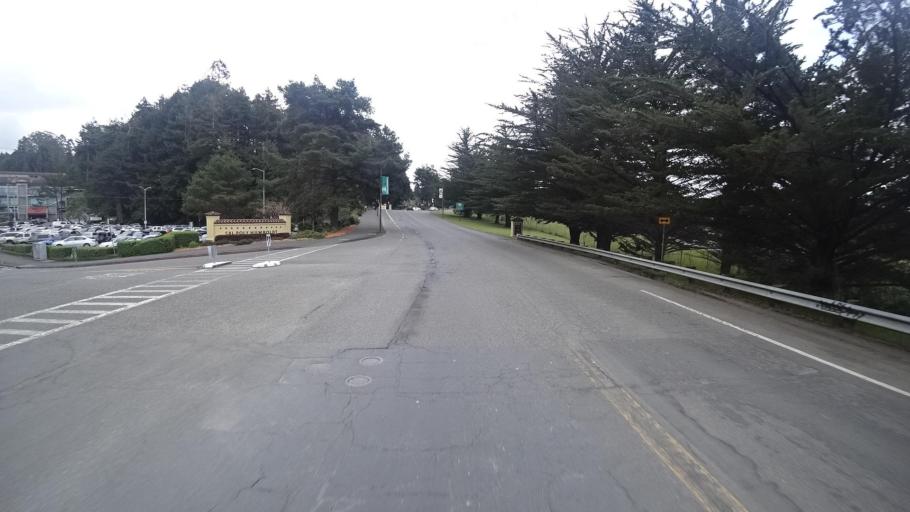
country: US
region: California
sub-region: Humboldt County
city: Arcata
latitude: 40.8800
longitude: -124.0811
